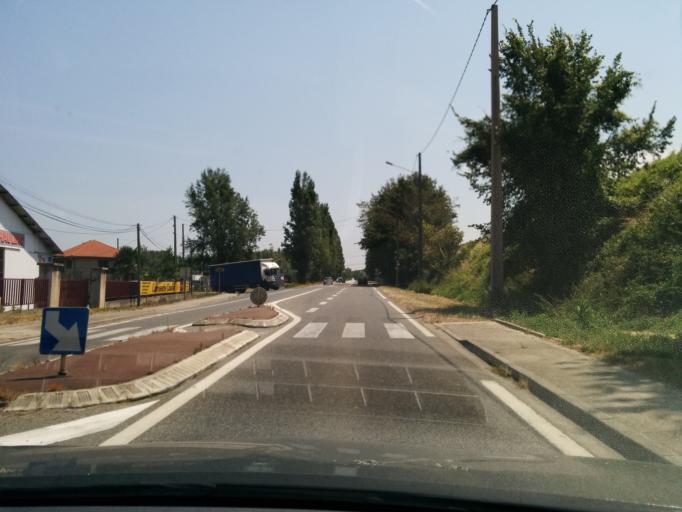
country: FR
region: Midi-Pyrenees
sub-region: Departement de la Haute-Garonne
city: Montgiscard
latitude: 43.4554
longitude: 1.5824
